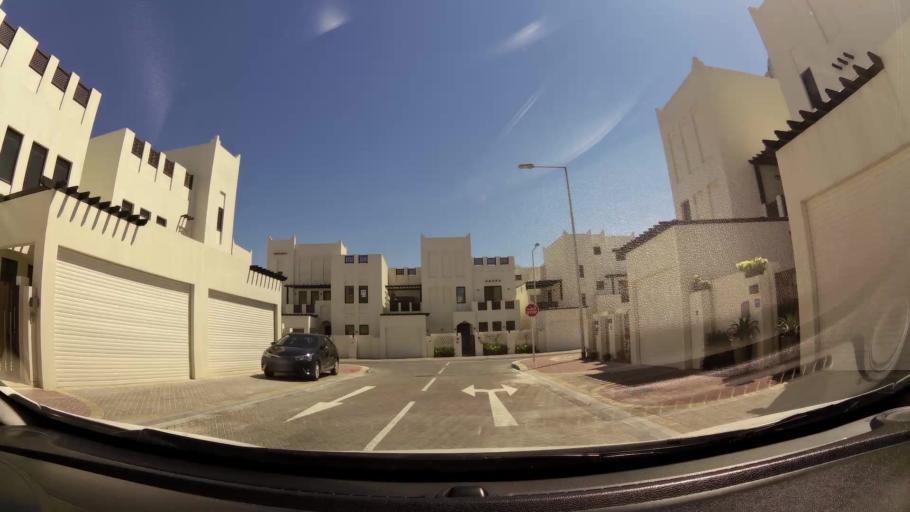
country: BH
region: Muharraq
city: Al Muharraq
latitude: 26.3017
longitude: 50.6366
